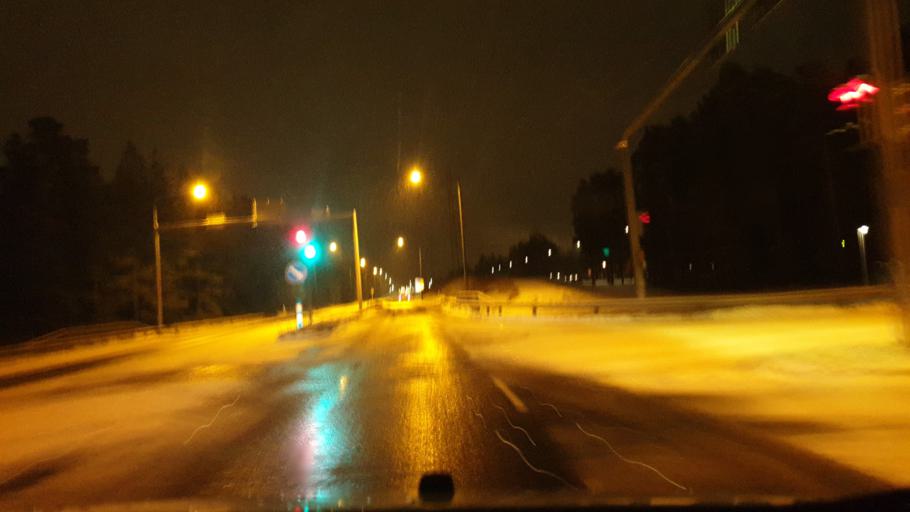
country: FI
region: Northern Ostrobothnia
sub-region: Oulu
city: Oulu
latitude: 64.9854
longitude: 25.4915
